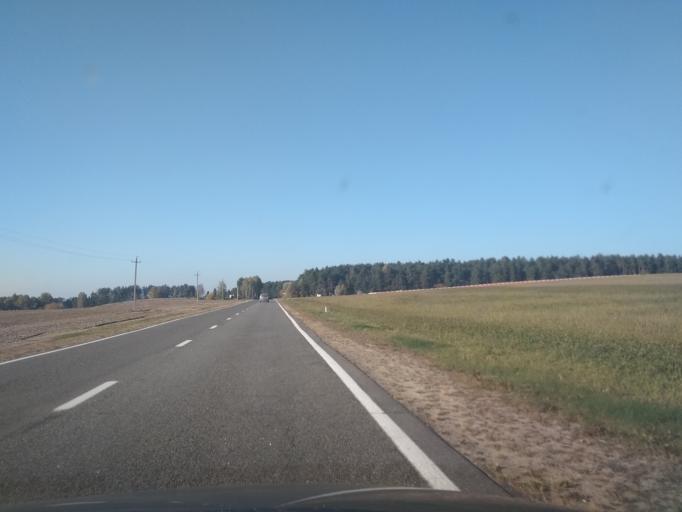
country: BY
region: Grodnenskaya
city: Vawkavysk
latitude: 53.1484
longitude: 24.5017
